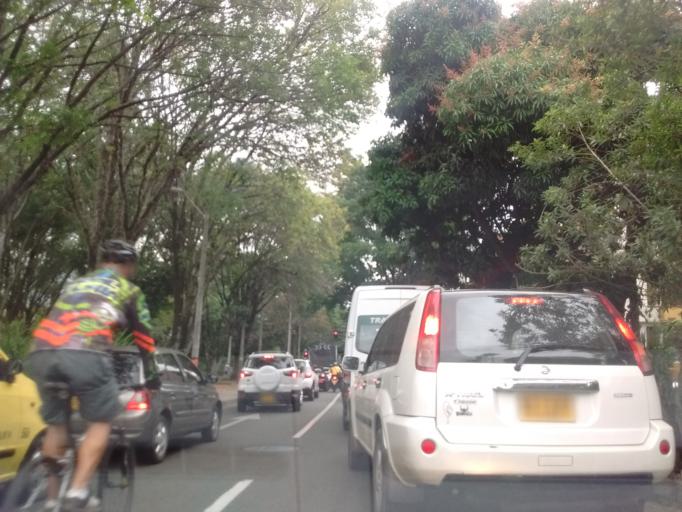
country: CO
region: Antioquia
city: Medellin
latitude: 6.2541
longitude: -75.5924
